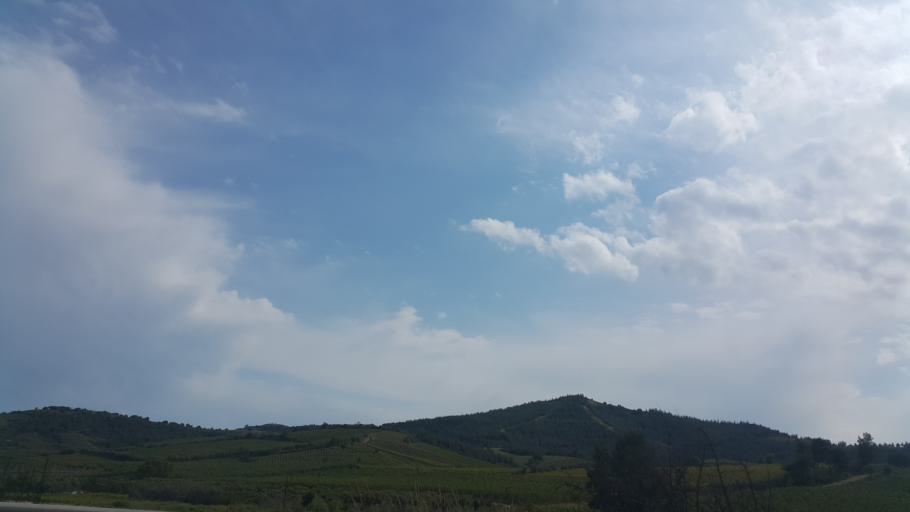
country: TR
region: Mersin
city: Tarsus
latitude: 36.9541
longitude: 34.7636
